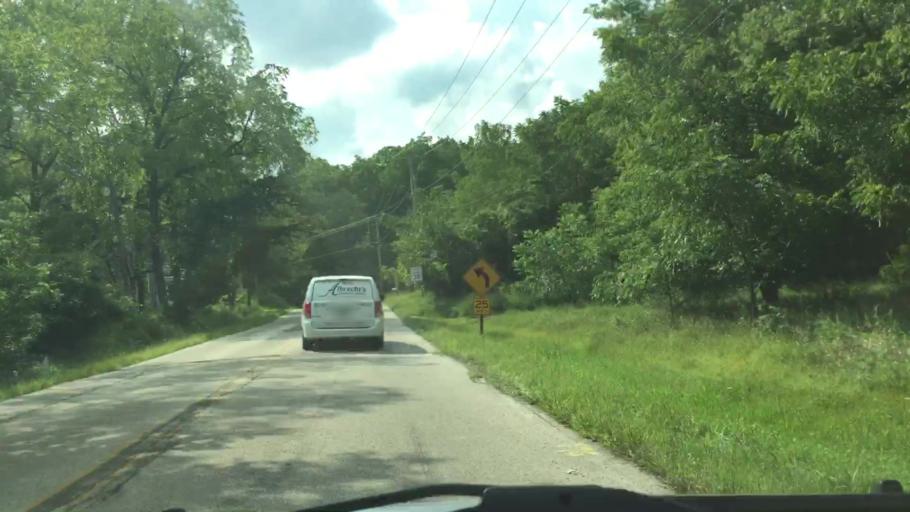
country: US
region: Wisconsin
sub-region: Waukesha County
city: Wales
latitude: 43.0407
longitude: -88.3500
